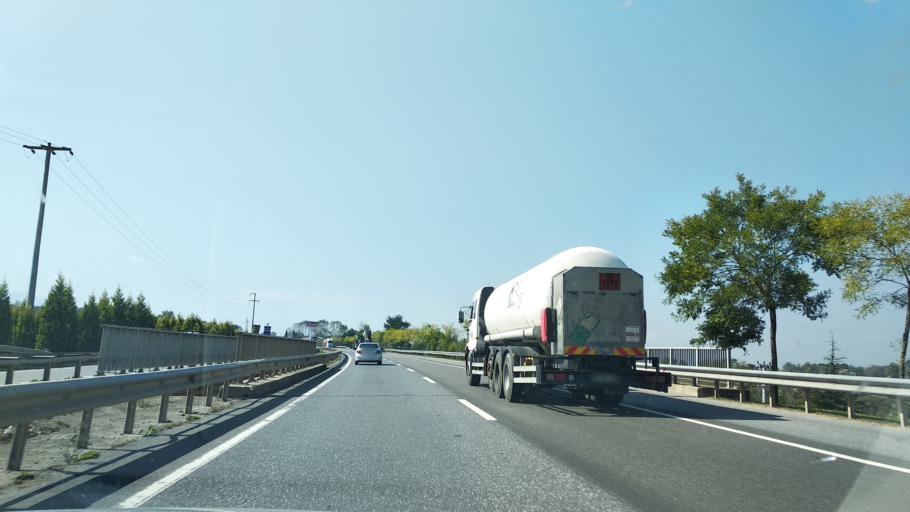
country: TR
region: Kocaeli
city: Derbent
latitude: 40.7311
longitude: 30.1564
